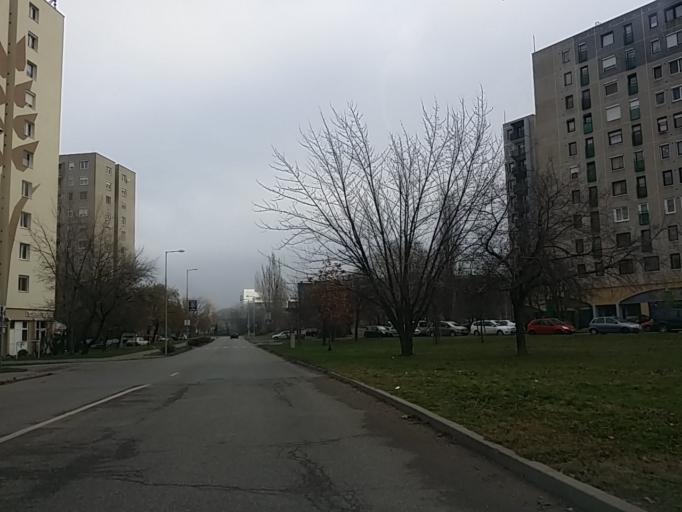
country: HU
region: Budapest
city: Budapest III. keruelet
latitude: 47.5527
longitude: 19.0403
